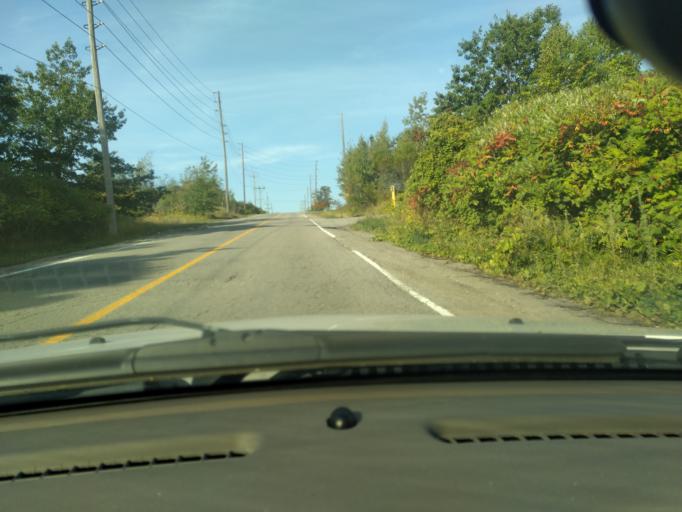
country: CA
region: Ontario
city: Innisfil
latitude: 44.3245
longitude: -79.6776
